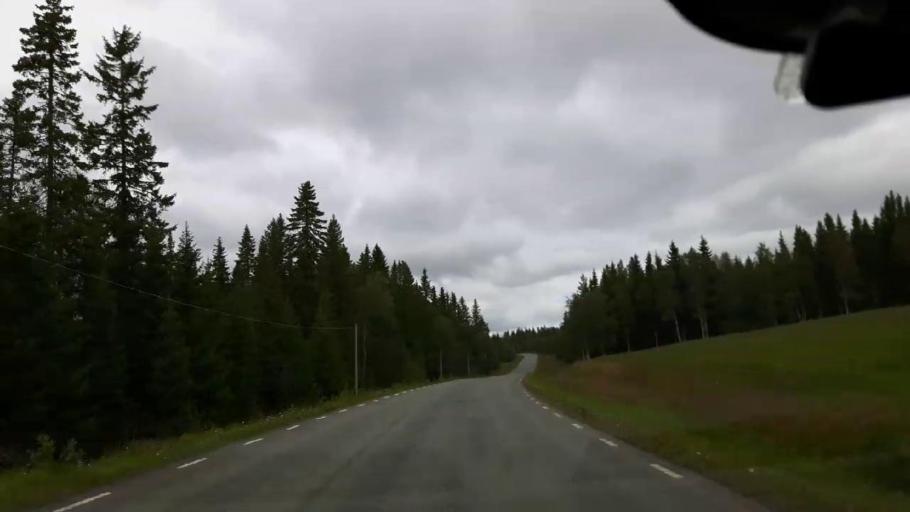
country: SE
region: Jaemtland
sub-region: Krokoms Kommun
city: Valla
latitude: 63.5147
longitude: 13.8778
